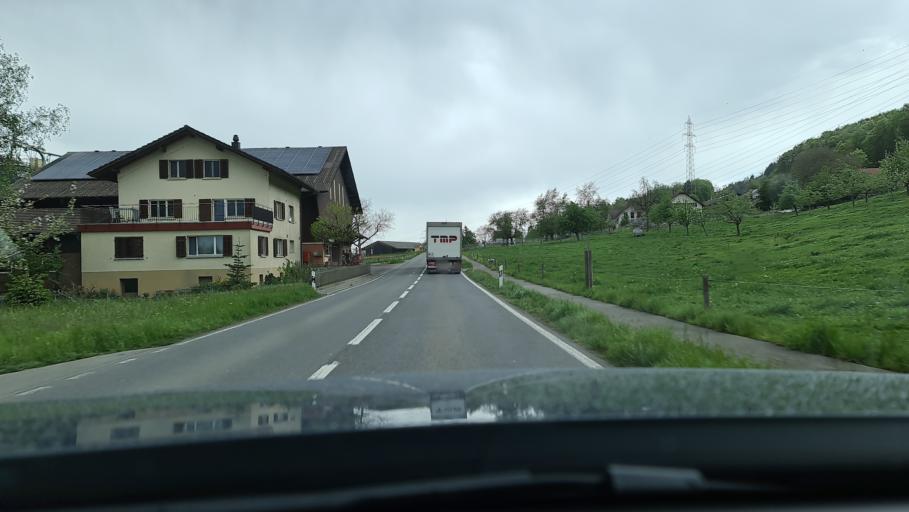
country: CH
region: Lucerne
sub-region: Sursee District
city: Triengen
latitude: 47.2510
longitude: 8.0671
